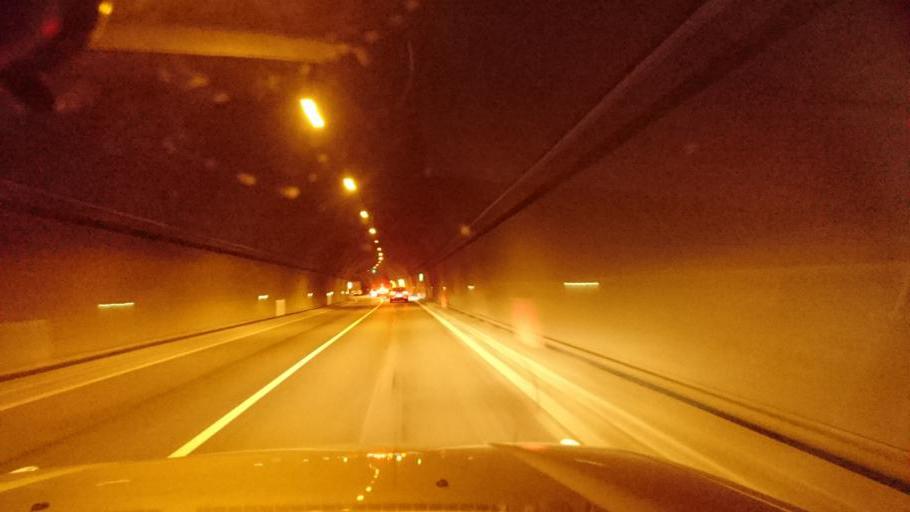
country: IT
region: Lombardy
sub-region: Provincia di Brescia
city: Roe Volciano
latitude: 45.6123
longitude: 10.4742
